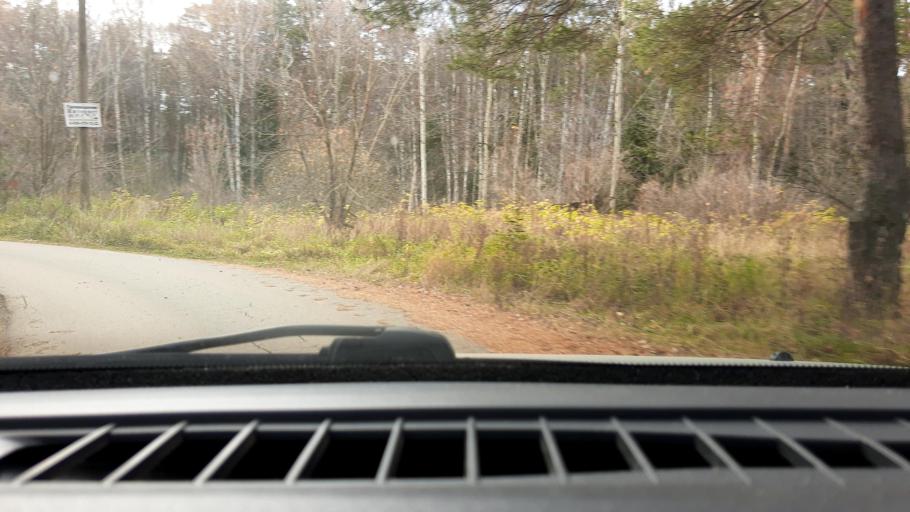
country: RU
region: Nizjnij Novgorod
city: Kstovo
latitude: 56.1700
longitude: 44.1254
